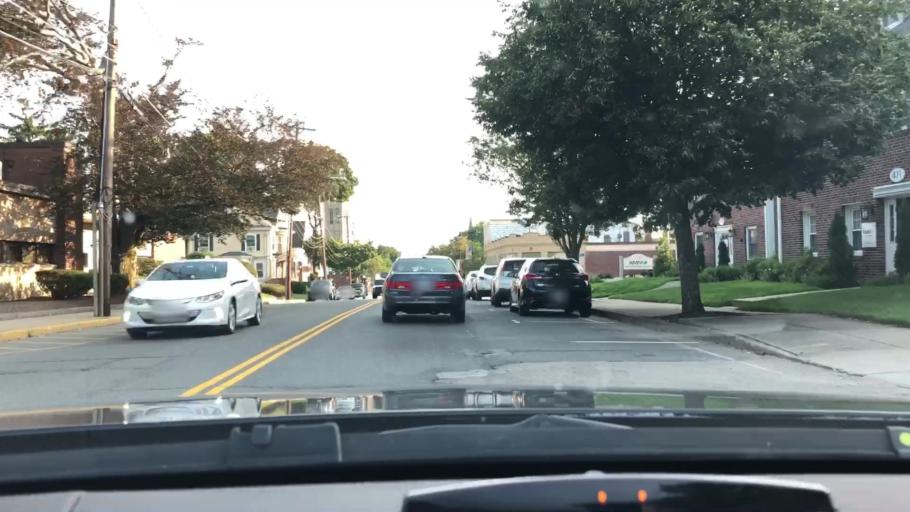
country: US
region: Massachusetts
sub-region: Norfolk County
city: Norwood
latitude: 42.1976
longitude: -71.1986
